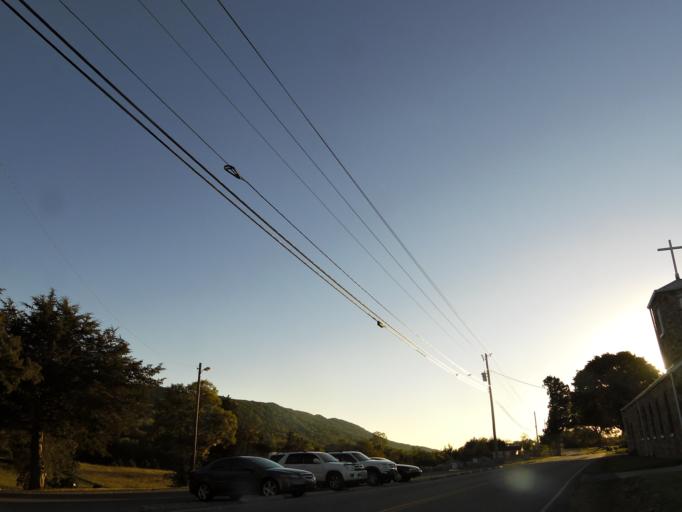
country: US
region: Tennessee
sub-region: Grainger County
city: Rutledge
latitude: 36.2907
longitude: -83.5951
